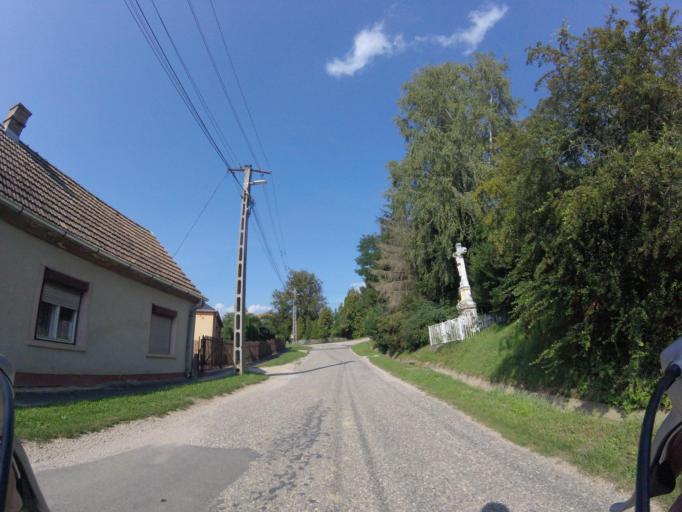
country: HU
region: Zala
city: Nagykanizsa
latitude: 46.5006
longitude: 17.0626
